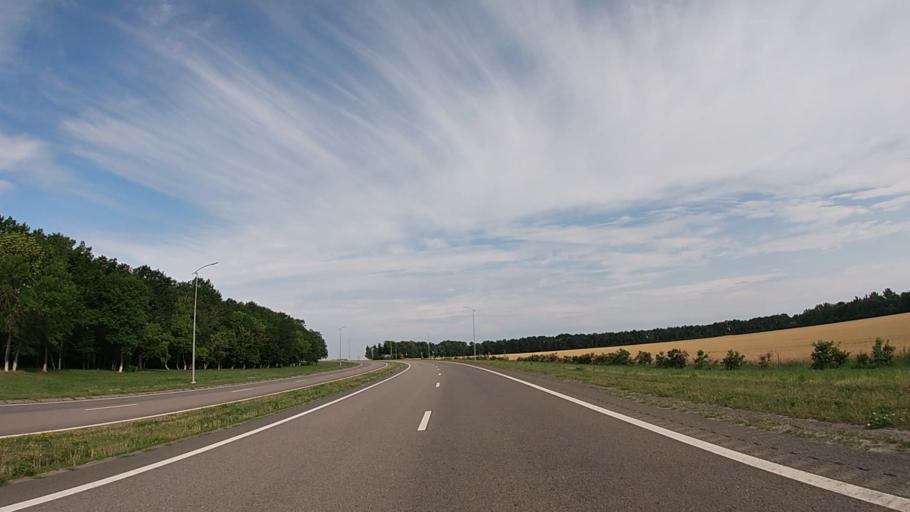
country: RU
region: Belgorod
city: Rakitnoye
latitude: 50.7610
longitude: 35.9623
